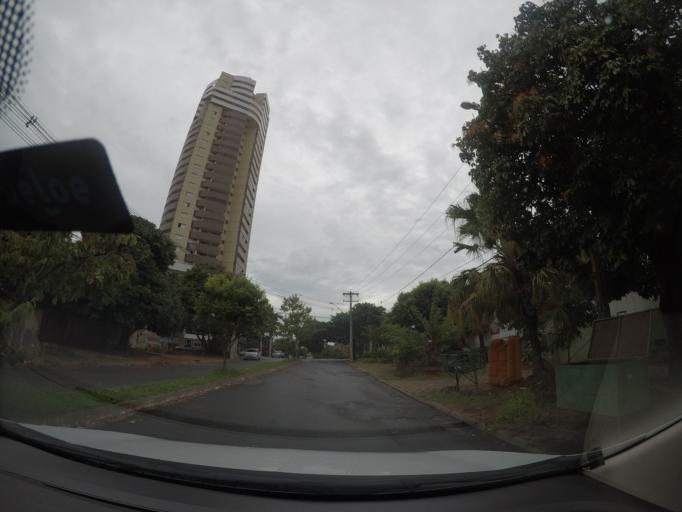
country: BR
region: Goias
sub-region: Goiania
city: Goiania
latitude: -16.6825
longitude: -49.2374
